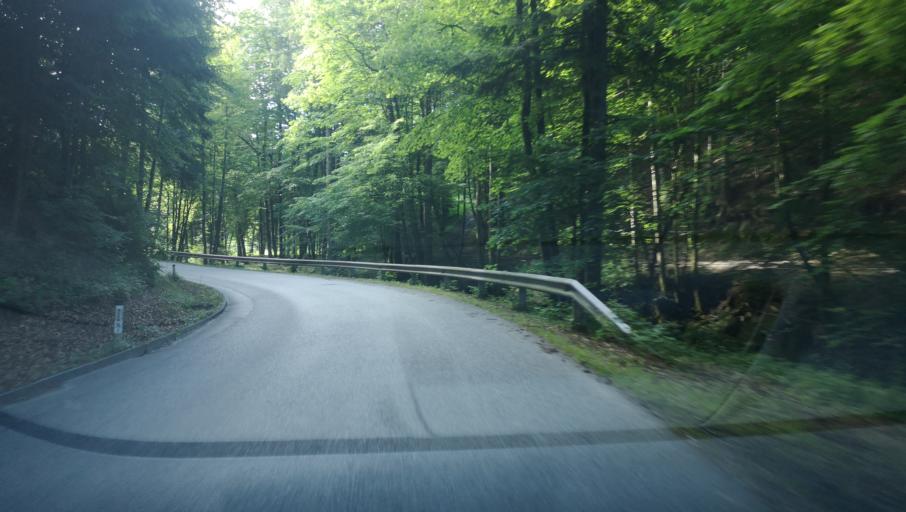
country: AT
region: Lower Austria
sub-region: Politischer Bezirk Scheibbs
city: Wang
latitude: 48.0310
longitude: 15.0268
